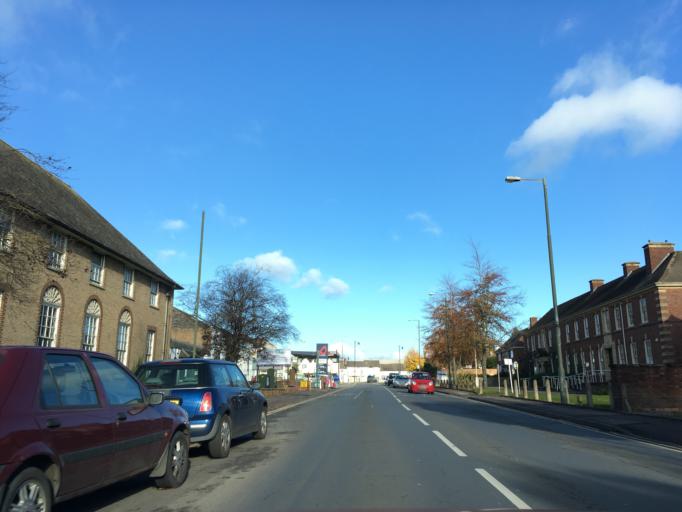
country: GB
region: England
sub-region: Worcestershire
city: Evesham
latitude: 52.0899
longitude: -1.9504
